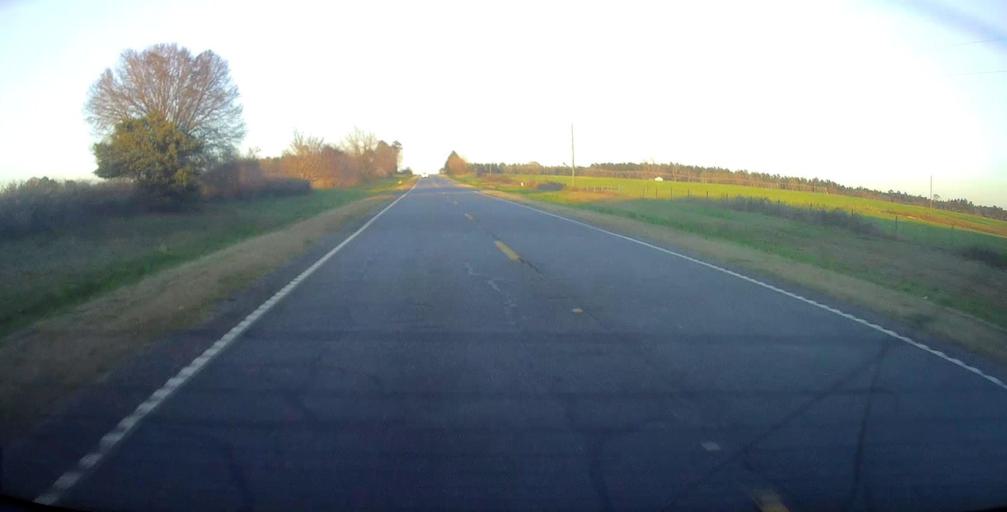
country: US
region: Georgia
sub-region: Dodge County
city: Chester
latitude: 32.2924
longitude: -83.0904
